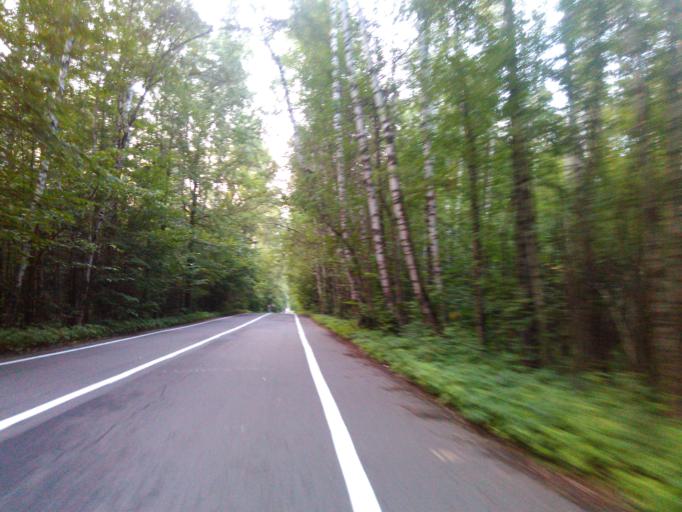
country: RU
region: Moscow
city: Babushkin
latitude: 55.8438
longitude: 37.7265
